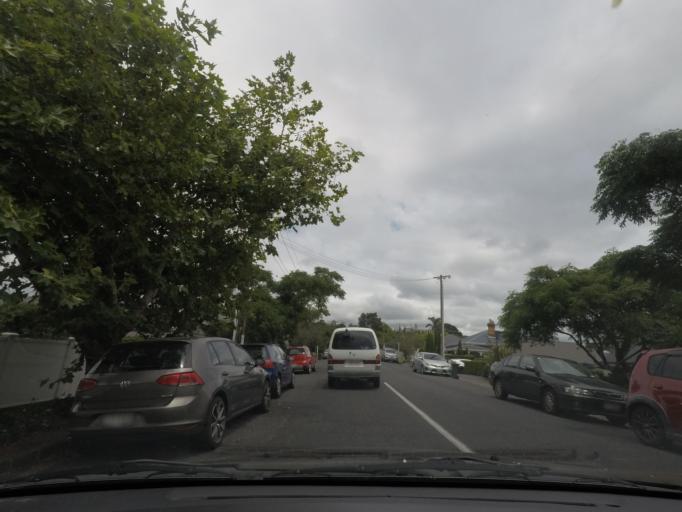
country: NZ
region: Auckland
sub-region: Auckland
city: Auckland
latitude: -36.8673
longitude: 174.7836
